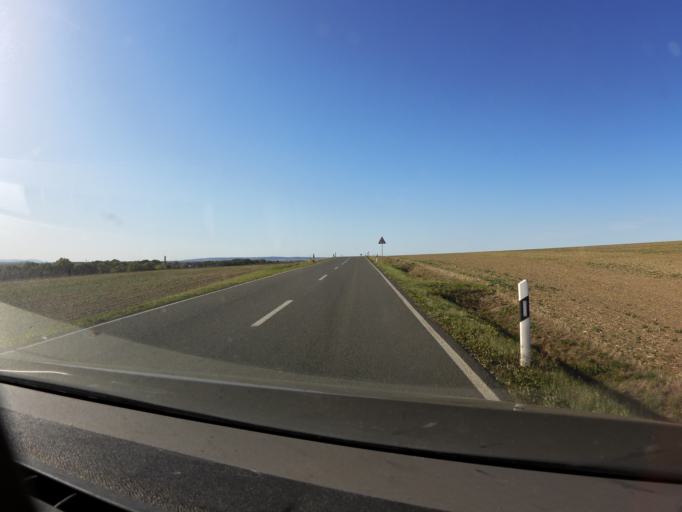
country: DE
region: Saxony-Anhalt
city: Hedersleben
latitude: 51.8727
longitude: 11.2370
